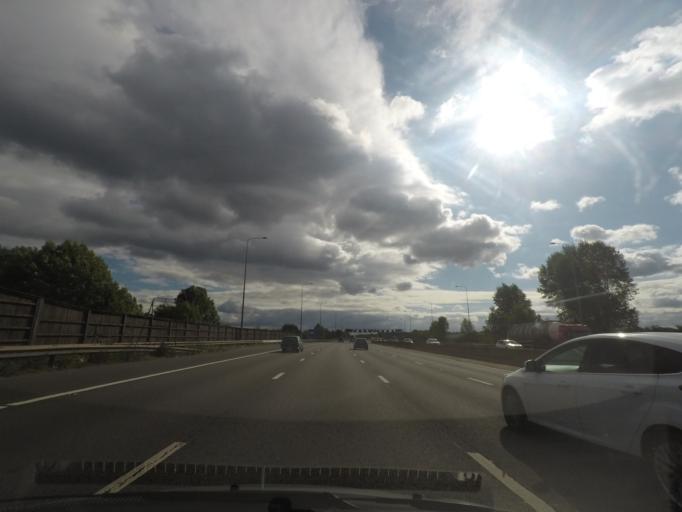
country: GB
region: England
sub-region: Derbyshire
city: Ilkeston
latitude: 52.9444
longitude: -1.2796
